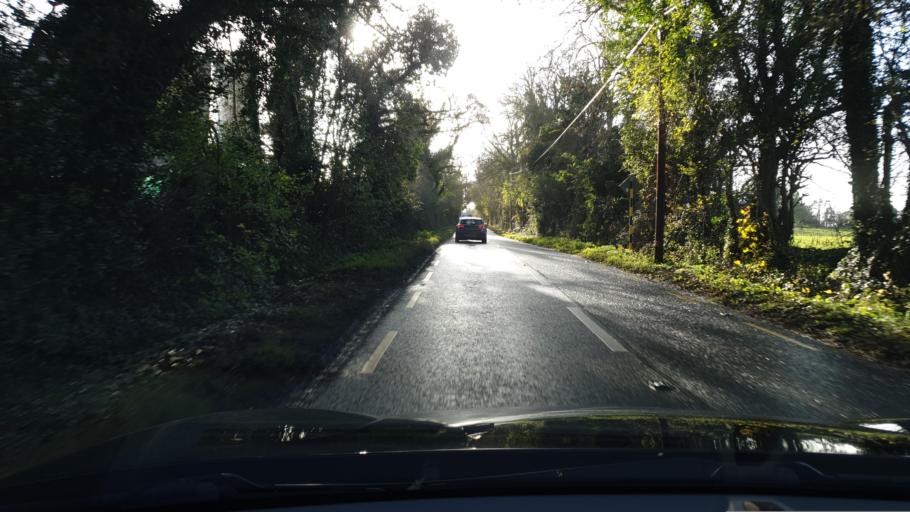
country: IE
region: Leinster
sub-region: Kildare
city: Leixlip
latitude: 53.3787
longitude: -6.5292
